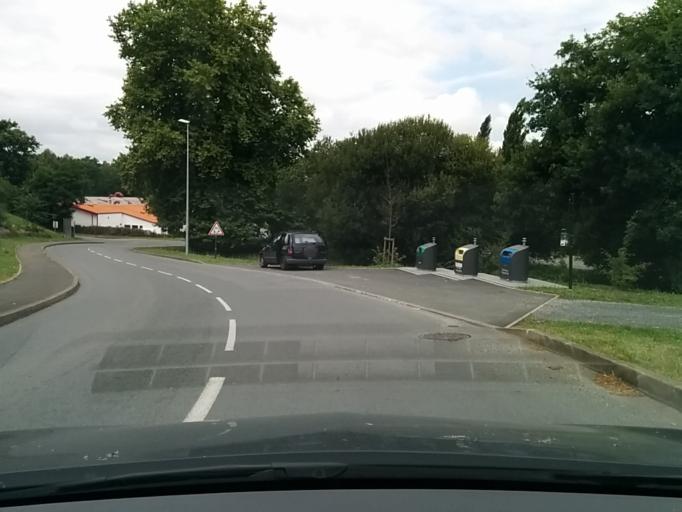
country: FR
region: Aquitaine
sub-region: Departement des Pyrenees-Atlantiques
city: Cambo-les-Bains
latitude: 43.3510
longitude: -1.4165
